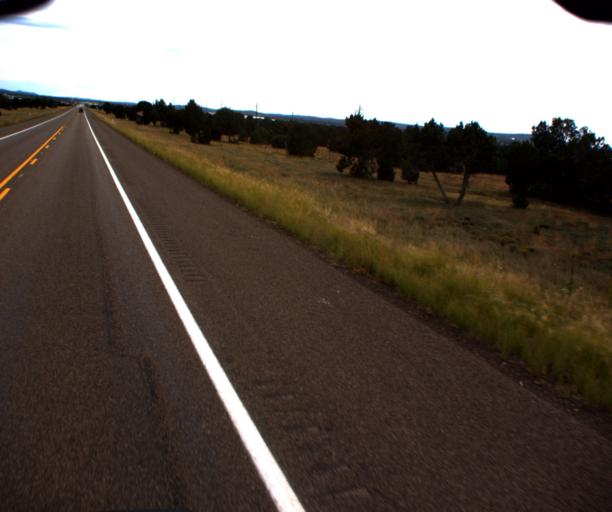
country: US
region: Arizona
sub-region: Navajo County
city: Show Low
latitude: 34.2848
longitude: -110.0289
